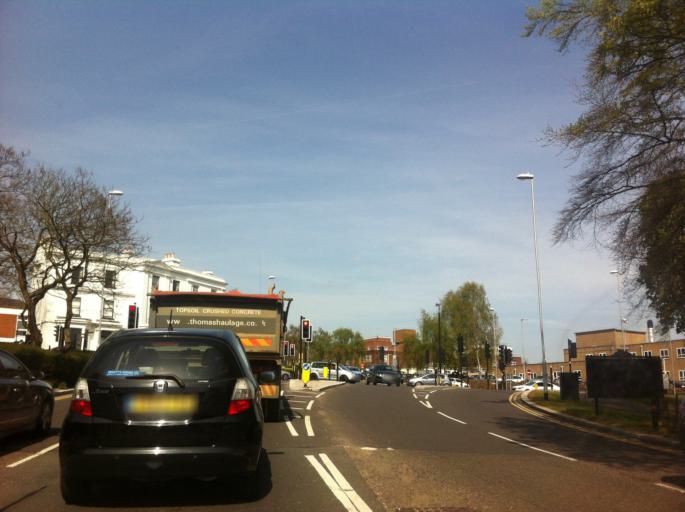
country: GB
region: England
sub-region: Northamptonshire
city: Northampton
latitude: 52.2351
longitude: -0.8898
